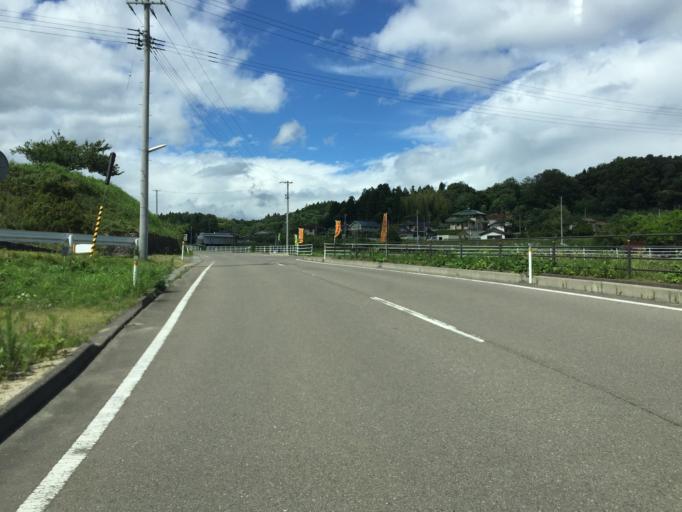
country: JP
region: Fukushima
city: Fukushima-shi
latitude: 37.6610
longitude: 140.5304
